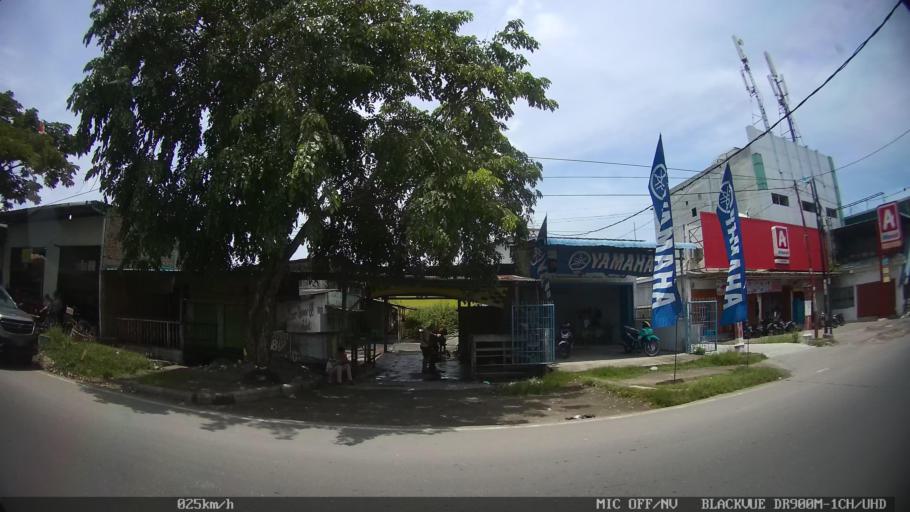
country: ID
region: North Sumatra
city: Belawan
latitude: 3.7729
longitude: 98.6814
